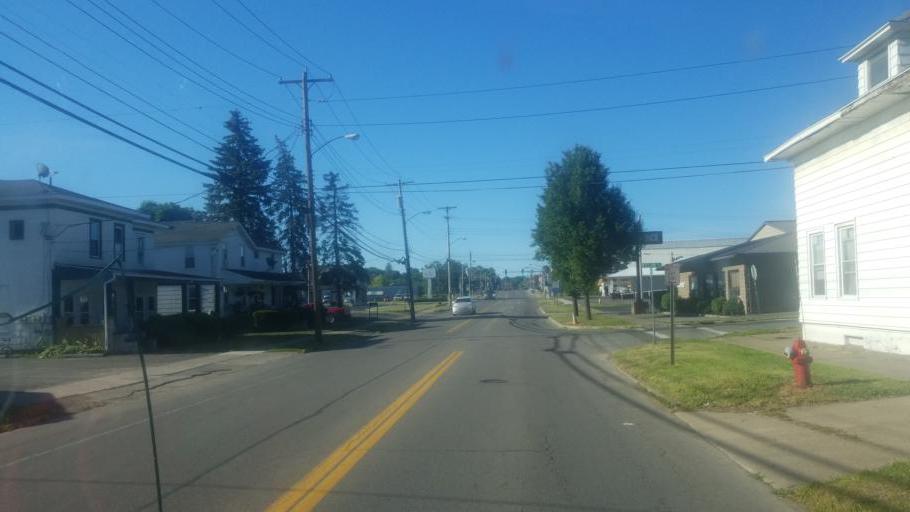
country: US
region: New York
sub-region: Wayne County
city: Newark
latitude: 43.0501
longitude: -77.0954
